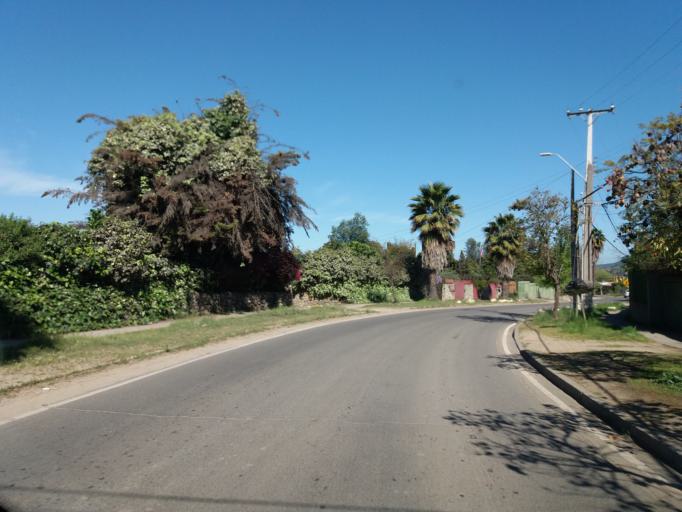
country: CL
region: Valparaiso
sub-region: Provincia de Marga Marga
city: Limache
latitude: -32.9941
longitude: -71.1693
